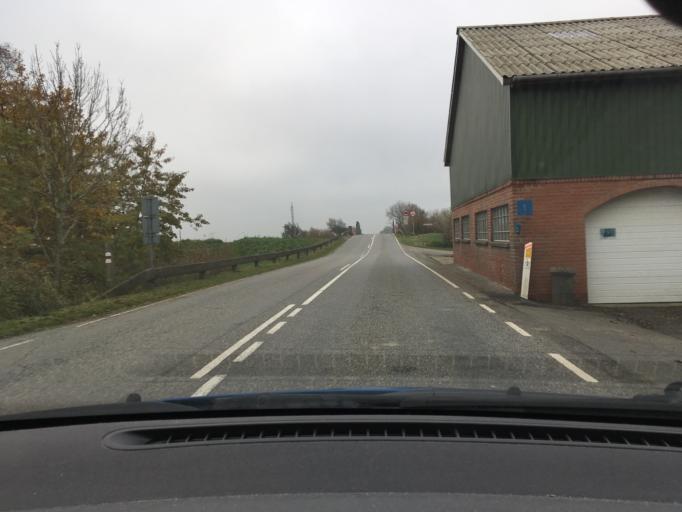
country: DE
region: Schleswig-Holstein
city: Aventoft
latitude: 54.9133
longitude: 8.8328
